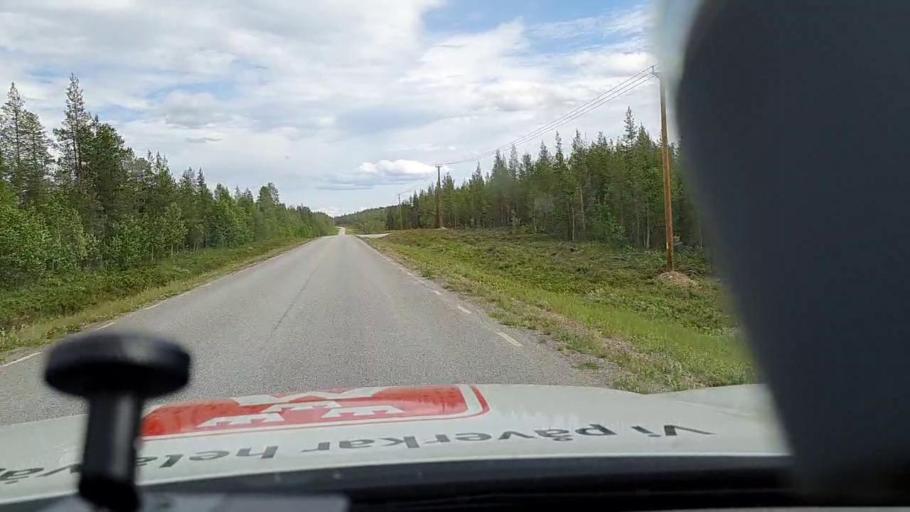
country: SE
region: Norrbotten
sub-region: Jokkmokks Kommun
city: Jokkmokk
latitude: 66.6566
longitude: 19.9748
